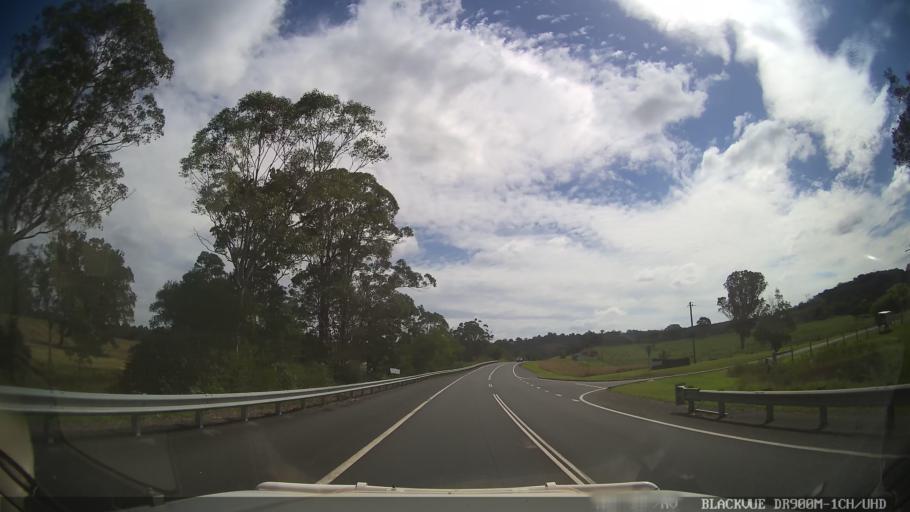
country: AU
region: Queensland
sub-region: Sunshine Coast
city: Nambour
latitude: -26.6198
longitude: 152.8850
